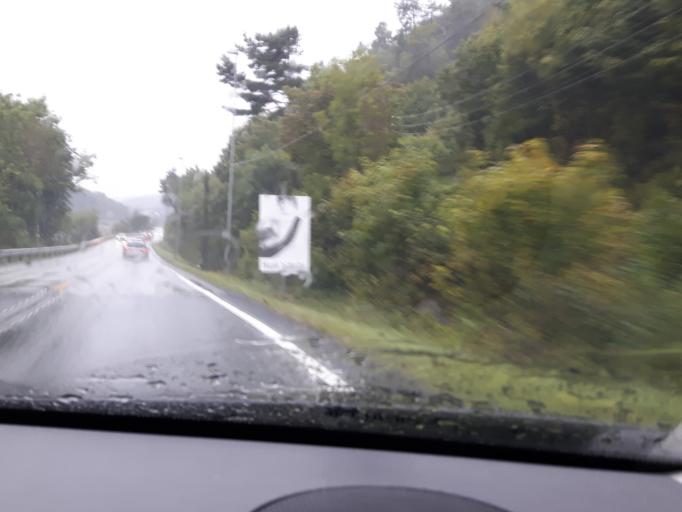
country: NO
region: Vest-Agder
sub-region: Mandal
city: Mandal
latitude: 58.0416
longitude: 7.4267
